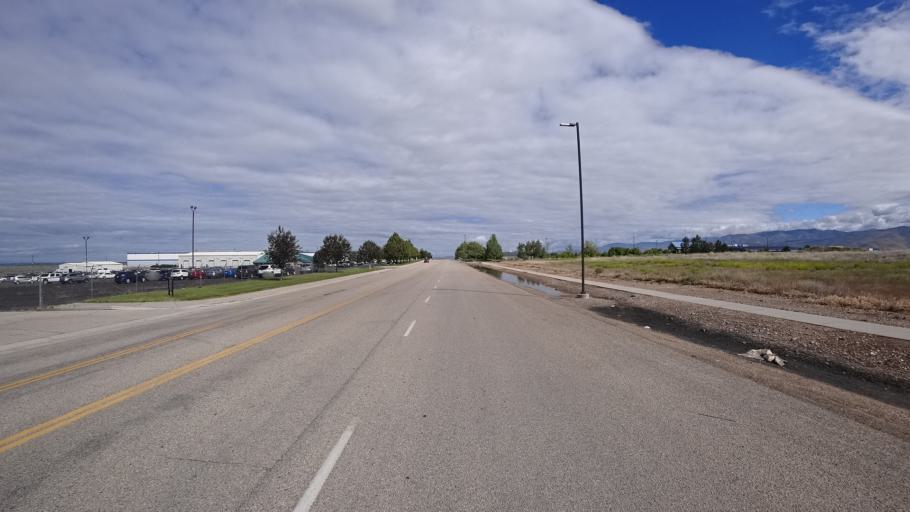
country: US
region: Idaho
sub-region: Ada County
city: Boise
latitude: 43.5349
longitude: -116.1604
